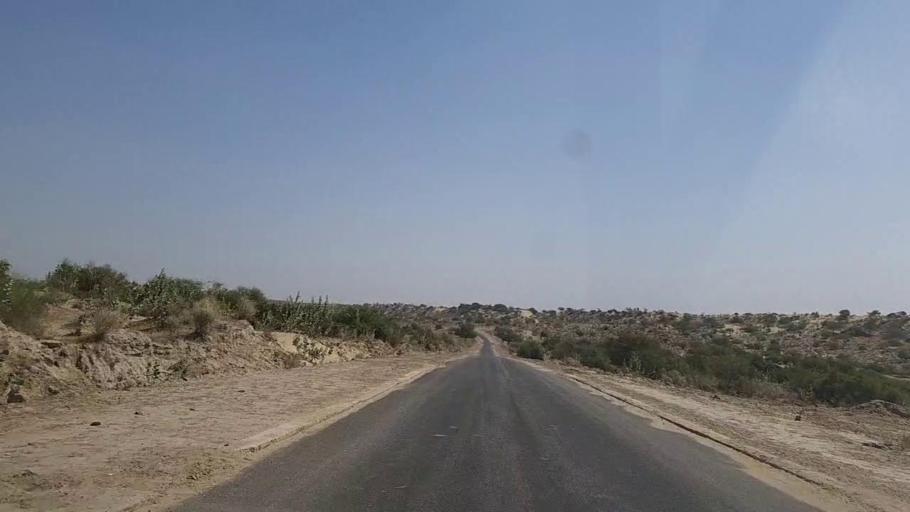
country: PK
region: Sindh
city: Diplo
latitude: 24.4820
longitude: 69.4809
